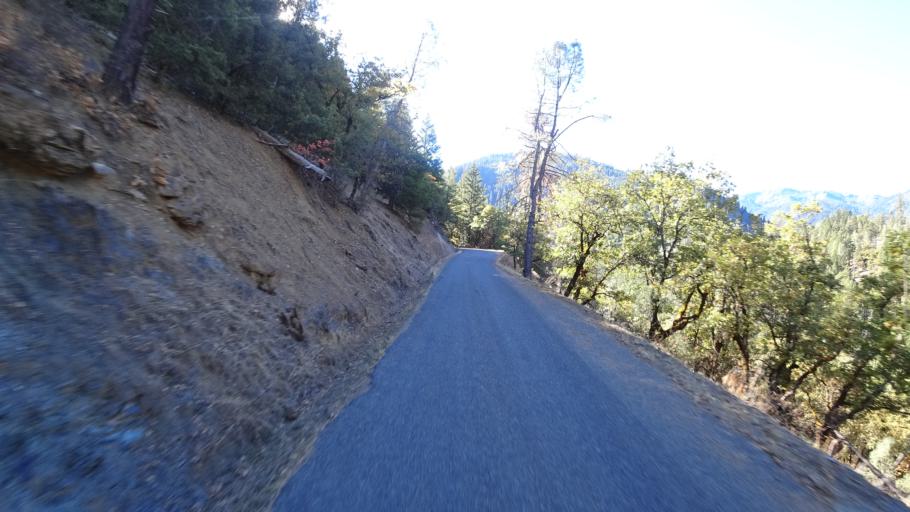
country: US
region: California
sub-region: Humboldt County
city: Willow Creek
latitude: 41.1555
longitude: -123.2094
